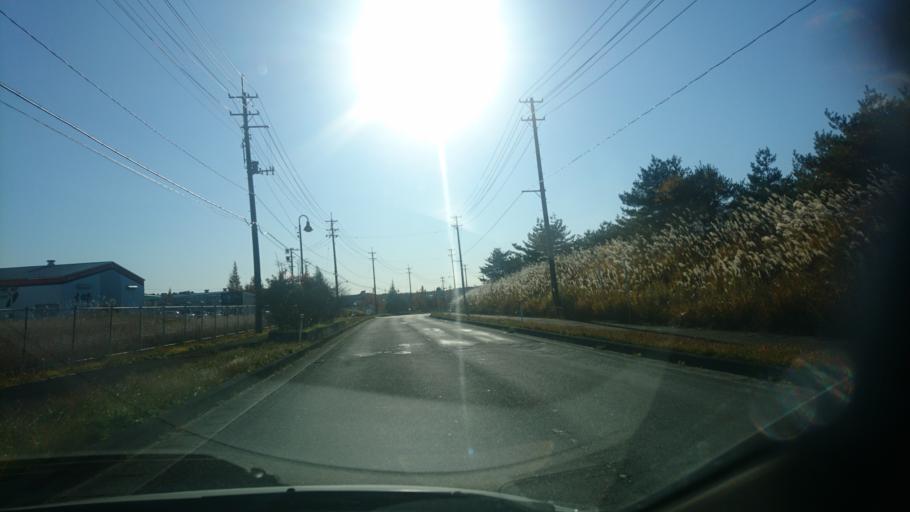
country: JP
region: Miyagi
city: Tomiya
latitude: 38.4547
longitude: 140.9332
